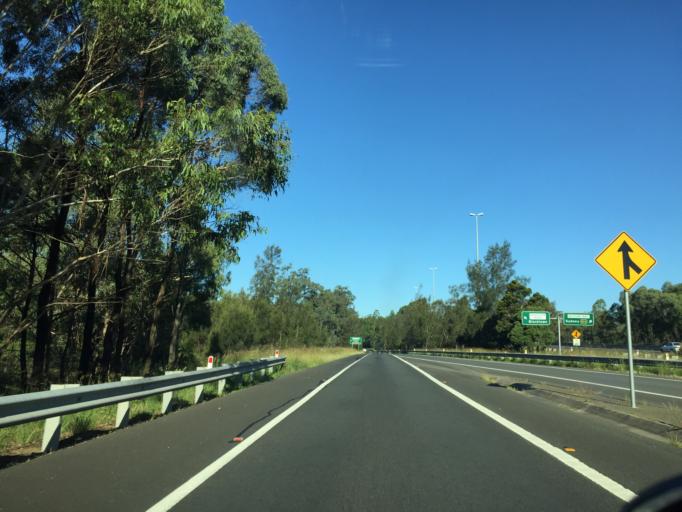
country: AU
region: New South Wales
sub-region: Blacktown
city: Doonside
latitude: -33.8022
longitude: 150.8911
